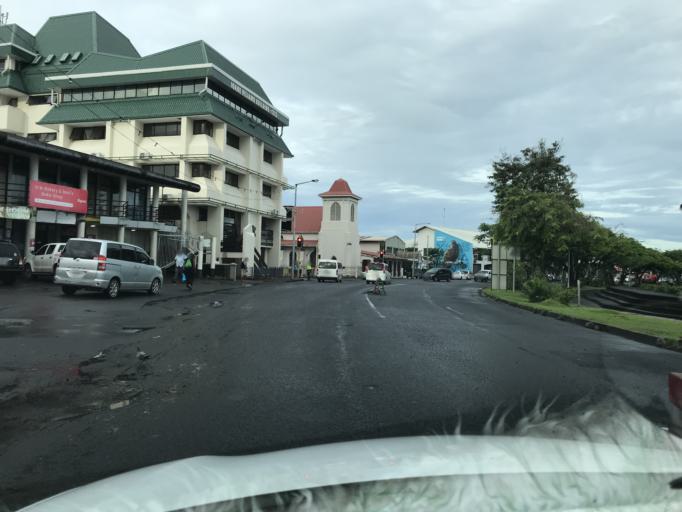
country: WS
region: Tuamasaga
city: Apia
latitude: -13.8332
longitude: -171.7617
